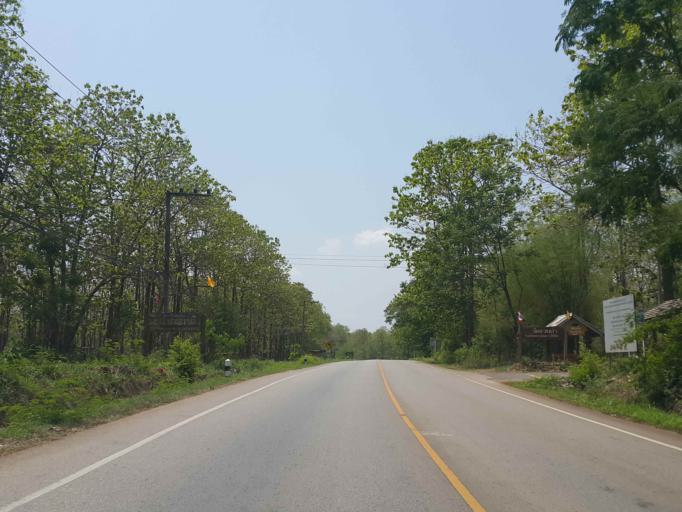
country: TH
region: Chiang Mai
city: Mae Taeng
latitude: 19.0945
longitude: 99.0834
